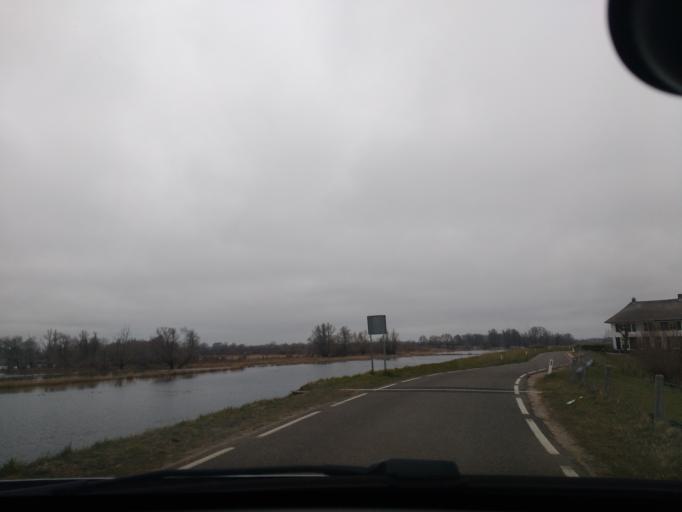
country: NL
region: Gelderland
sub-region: Gemeente Groesbeek
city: Berg en Dal
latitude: 51.8569
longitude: 5.9012
